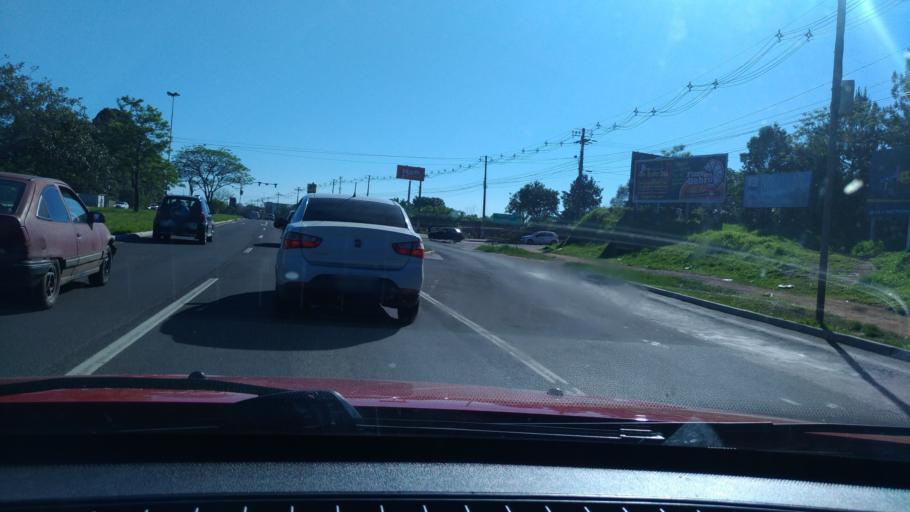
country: BR
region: Rio Grande do Sul
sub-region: Viamao
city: Viamao
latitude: -30.0867
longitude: -51.0575
